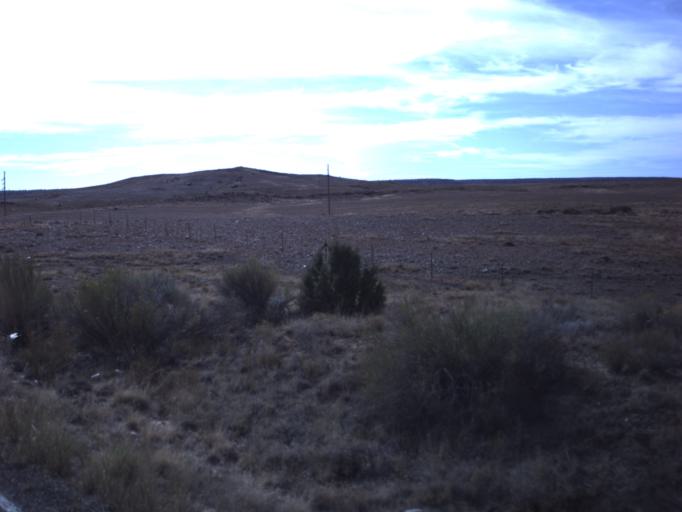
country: US
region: Utah
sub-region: San Juan County
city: Blanding
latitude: 37.4194
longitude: -109.4361
